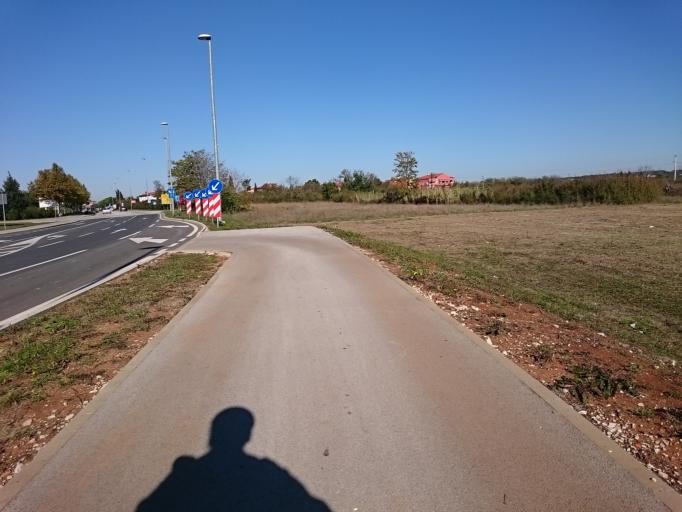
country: HR
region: Istarska
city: Umag
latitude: 45.4314
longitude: 13.5308
